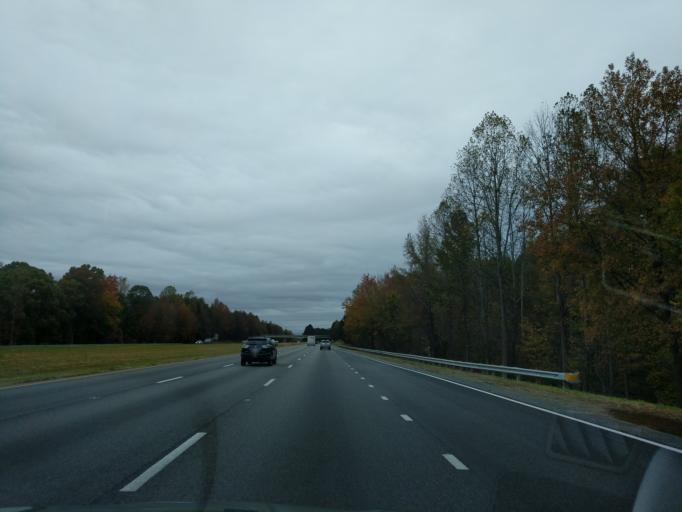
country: US
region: North Carolina
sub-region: Davidson County
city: Lexington
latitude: 35.8135
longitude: -80.1784
